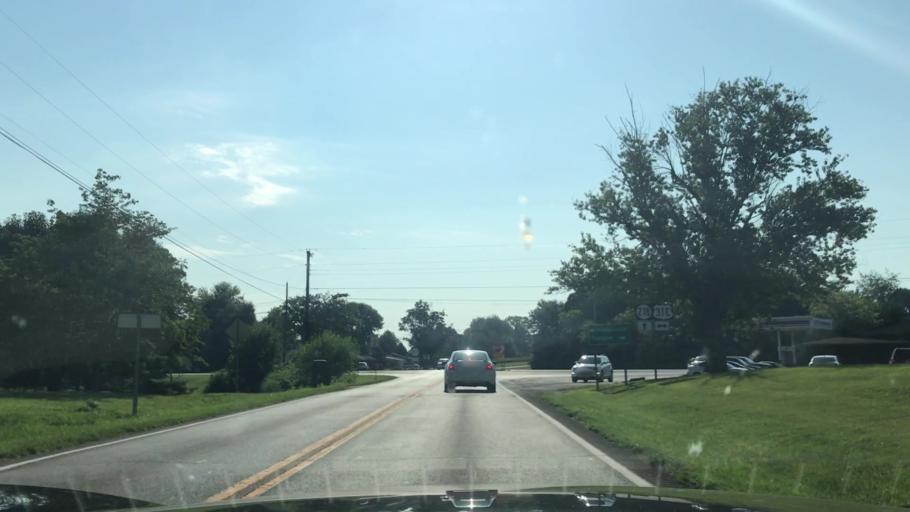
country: US
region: Kentucky
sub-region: Hart County
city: Horse Cave
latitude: 37.1666
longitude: -85.8410
